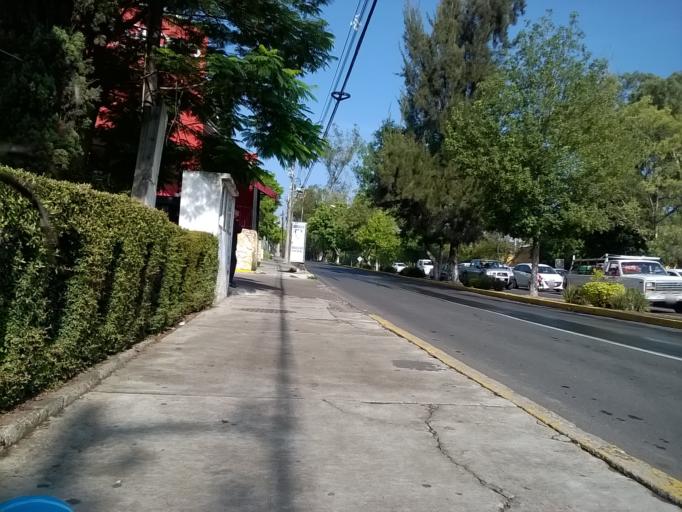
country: MX
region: Michoacan
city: Morelia
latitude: 19.6811
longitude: -101.1816
